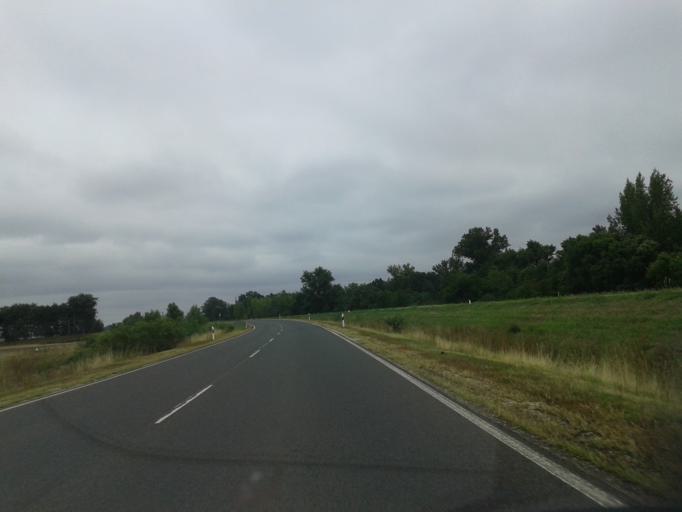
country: HU
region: Bacs-Kiskun
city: Harta
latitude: 46.7251
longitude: 19.0176
